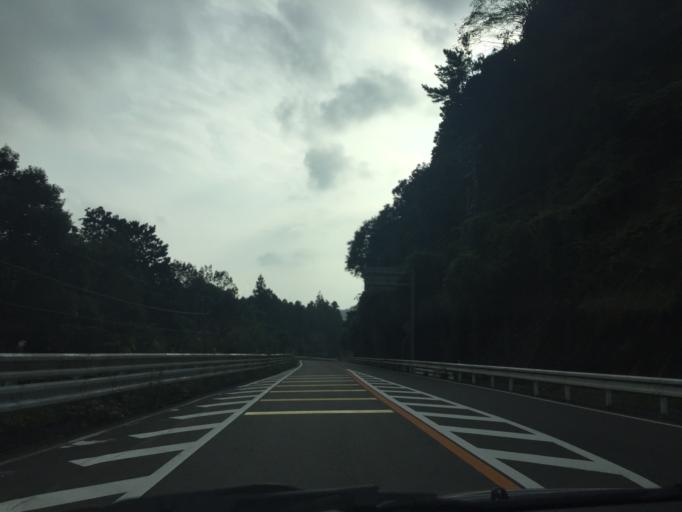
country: JP
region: Aichi
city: Shinshiro
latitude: 34.9416
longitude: 137.5937
